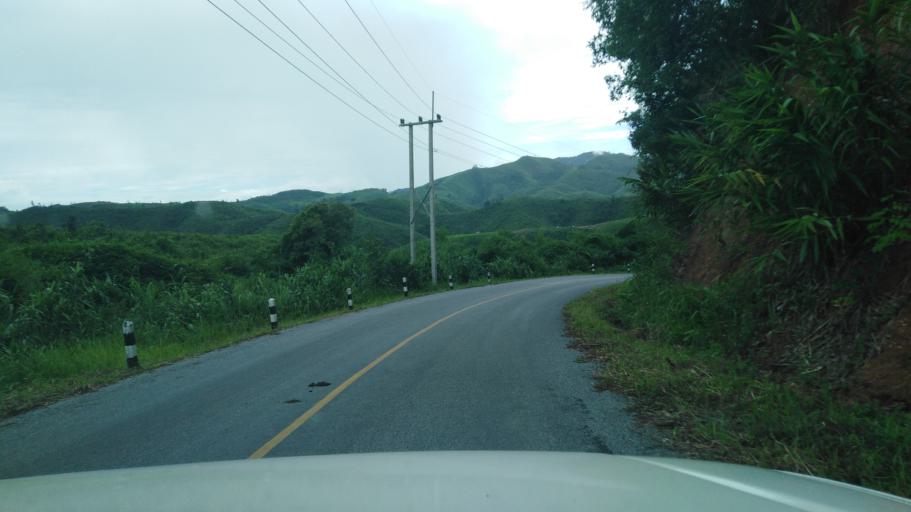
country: TH
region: Nan
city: Chaloem Phra Kiat
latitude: 19.6640
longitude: 100.9521
